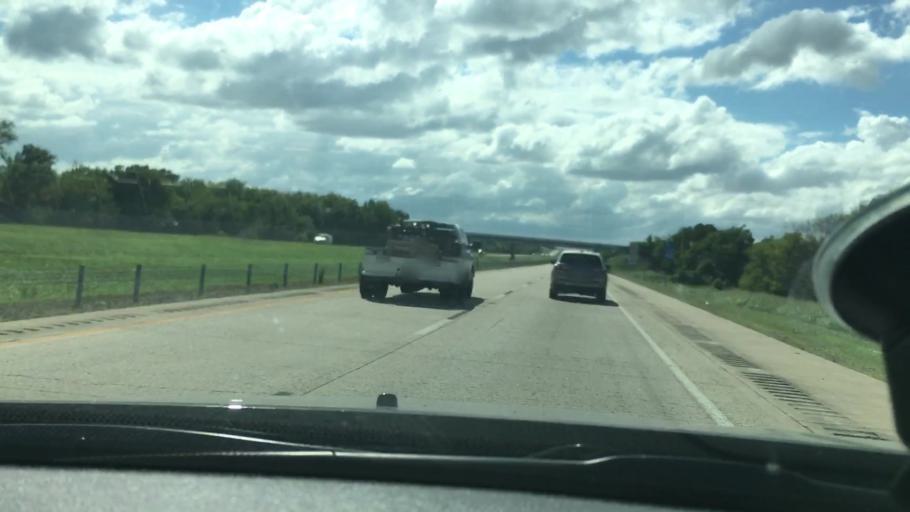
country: US
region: Oklahoma
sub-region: McIntosh County
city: Checotah
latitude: 35.4572
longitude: -95.5547
